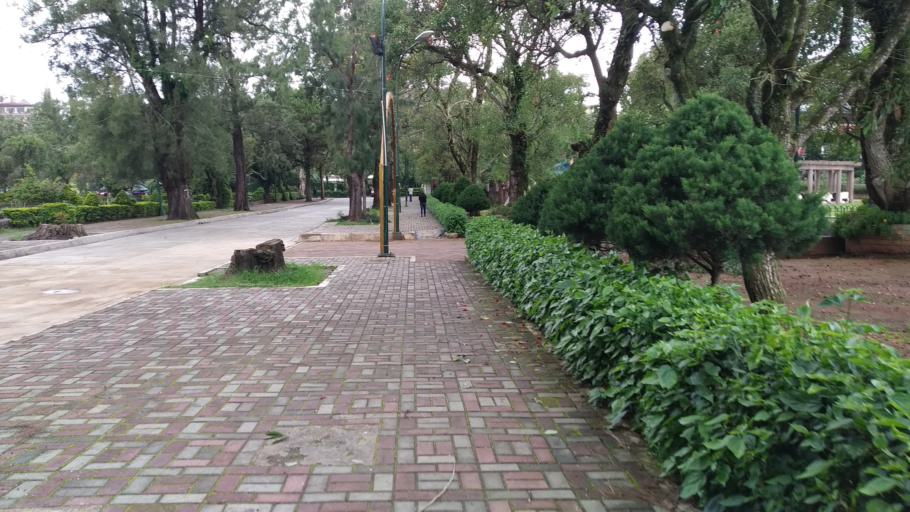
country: PH
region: Cordillera
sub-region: Baguio City
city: Baguio
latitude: 16.4117
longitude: 120.5938
